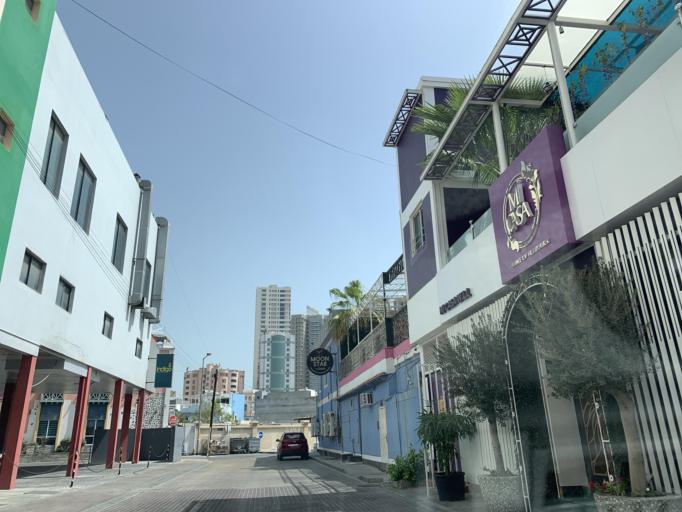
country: BH
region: Manama
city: Manama
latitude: 26.2129
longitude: 50.5948
